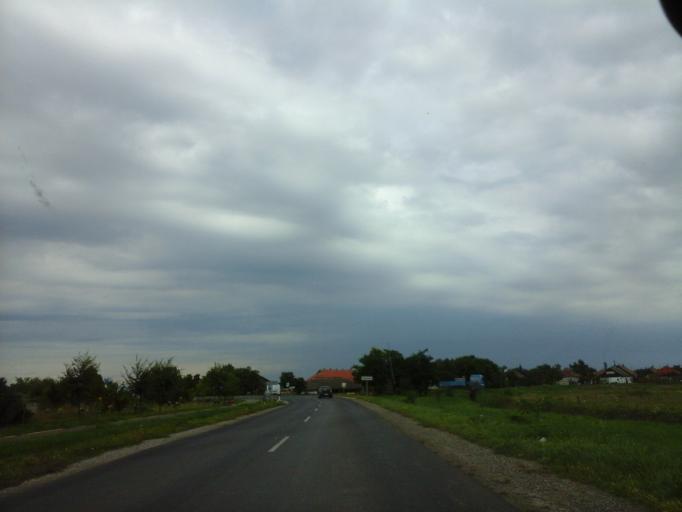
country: HU
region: Hajdu-Bihar
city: Balmazujvaros
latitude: 47.5985
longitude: 21.3381
